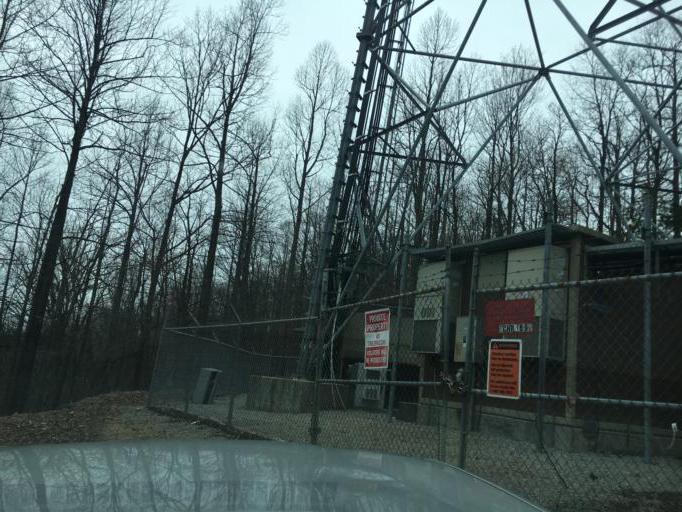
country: US
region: North Carolina
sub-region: Henderson County
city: East Flat Rock
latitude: 35.2575
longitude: -82.4168
